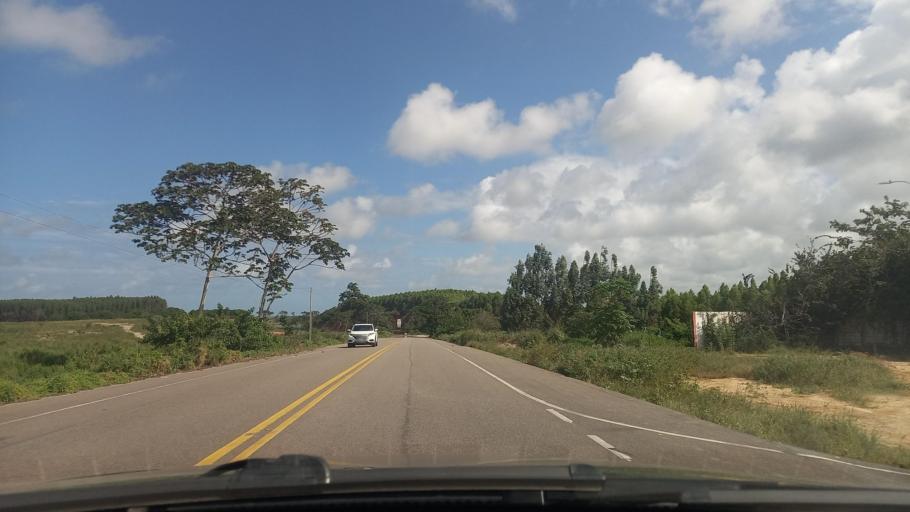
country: BR
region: Alagoas
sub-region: Marechal Deodoro
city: Marechal Deodoro
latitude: -9.8267
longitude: -35.9281
